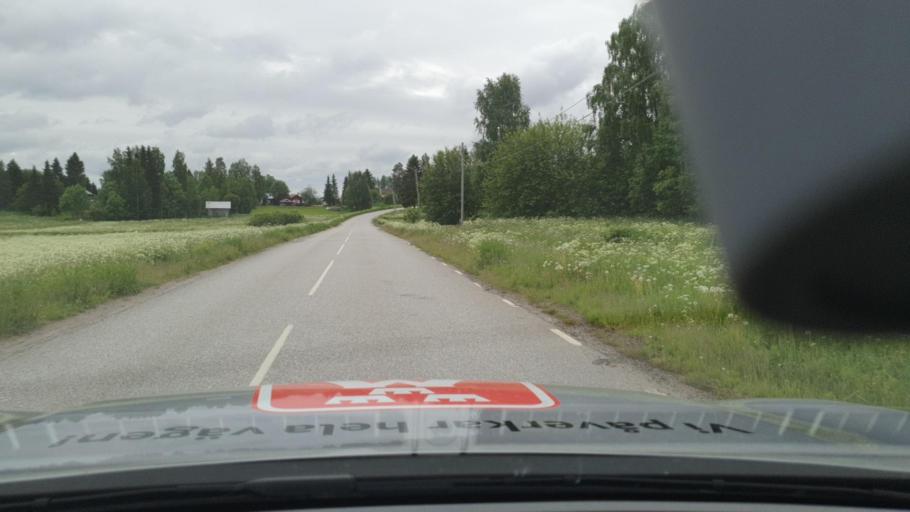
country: SE
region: Norrbotten
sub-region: Lulea Kommun
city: Ranea
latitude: 65.9054
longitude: 22.1786
